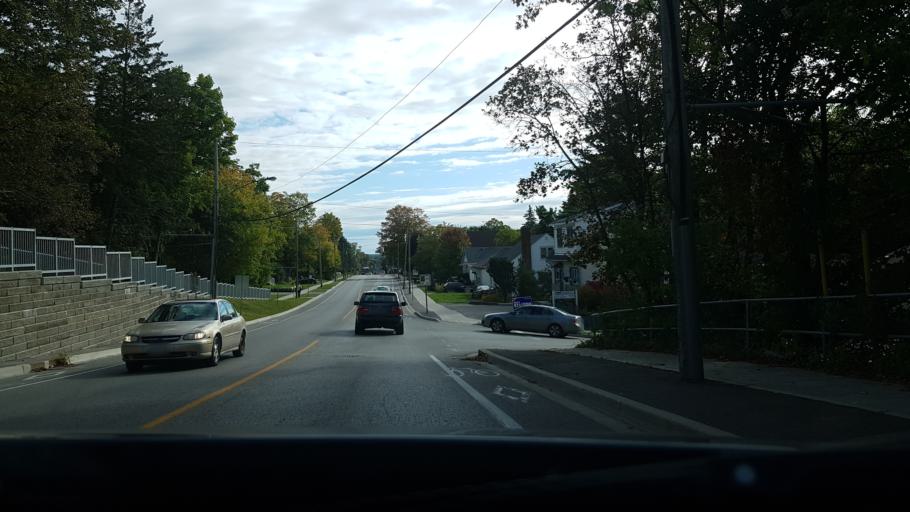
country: CA
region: Ontario
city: Orillia
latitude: 44.6091
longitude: -79.4315
